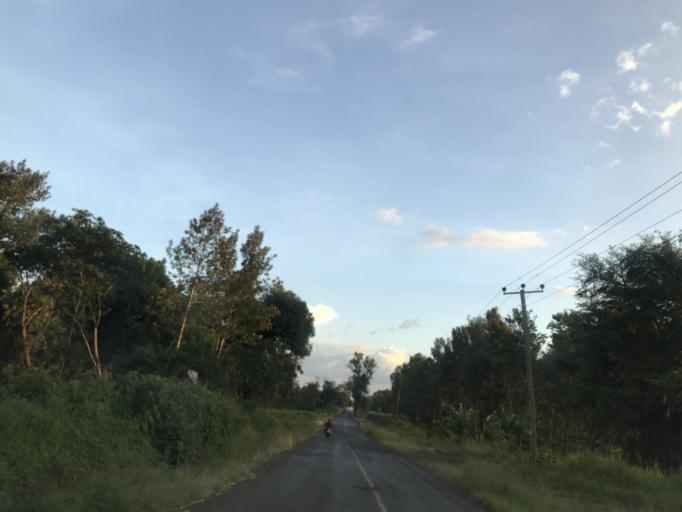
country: TZ
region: Arusha
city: Usa River
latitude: -3.3553
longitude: 36.8651
